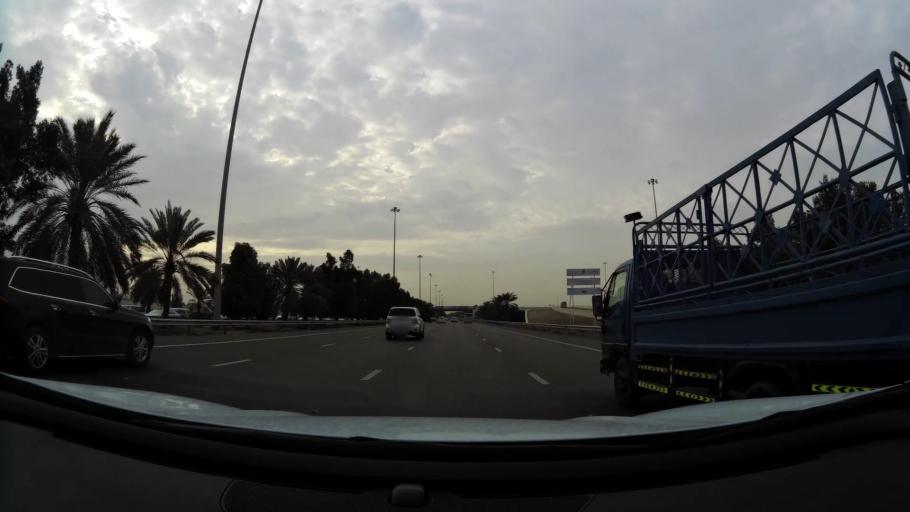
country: AE
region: Abu Dhabi
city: Abu Dhabi
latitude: 24.3547
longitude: 54.5677
